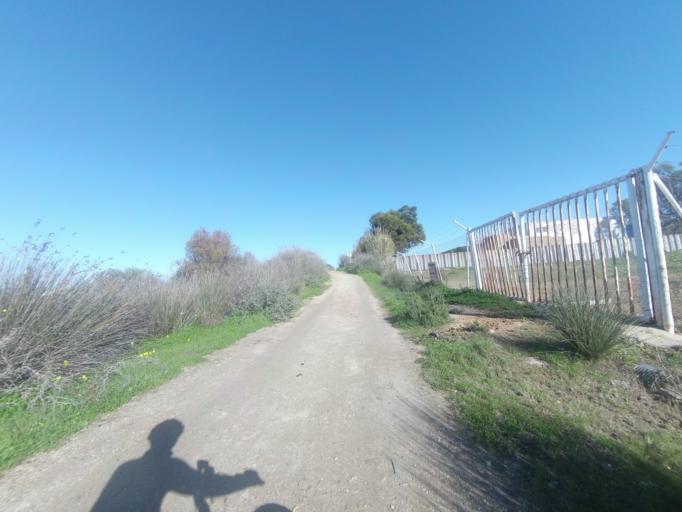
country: ES
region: Andalusia
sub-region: Provincia de Huelva
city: Palos de la Frontera
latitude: 37.2432
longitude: -6.8879
